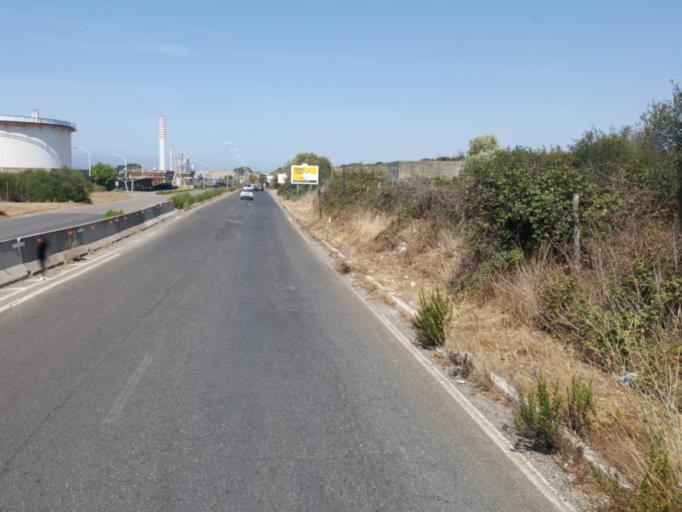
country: IT
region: Latium
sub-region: Citta metropolitana di Roma Capitale
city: Civitavecchia
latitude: 42.1101
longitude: 11.7847
